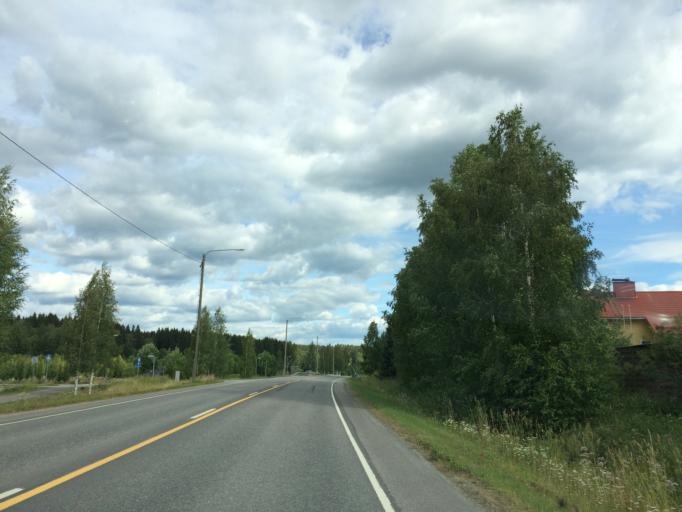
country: FI
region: Haeme
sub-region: Haemeenlinna
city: Turenki
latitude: 60.9556
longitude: 24.5992
